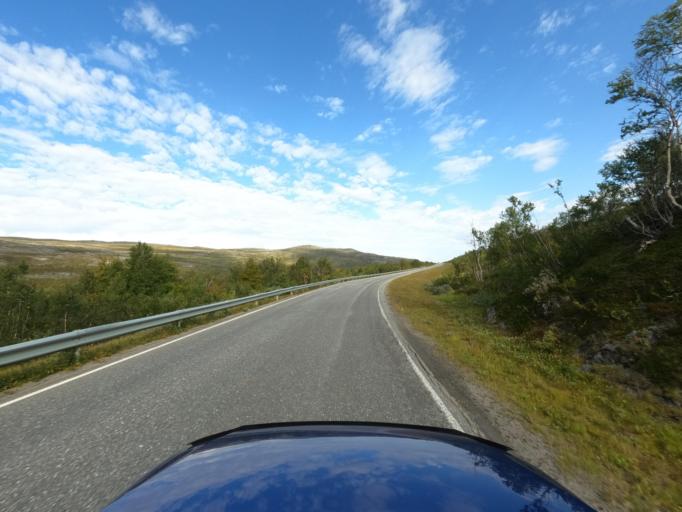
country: NO
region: Finnmark Fylke
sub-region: Kvalsund
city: Kvalsund
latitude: 70.3566
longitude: 24.3568
